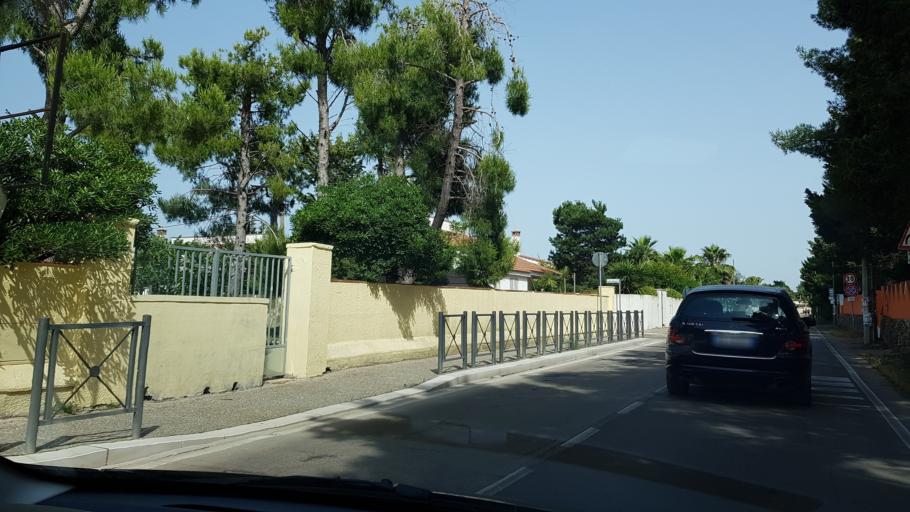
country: IT
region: Apulia
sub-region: Provincia di Lecce
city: Porto Cesareo
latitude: 40.2858
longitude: 17.8610
